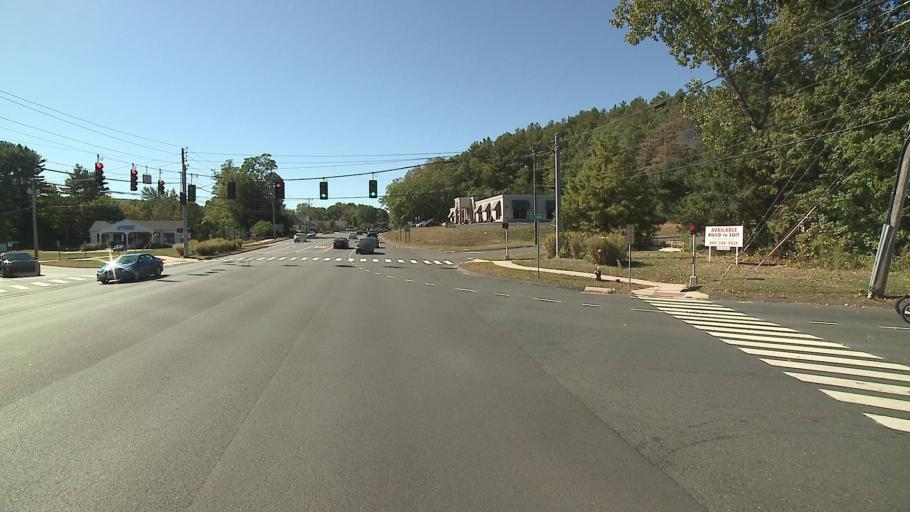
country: US
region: Connecticut
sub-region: Hartford County
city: Canton Valley
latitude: 41.8241
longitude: -72.8873
